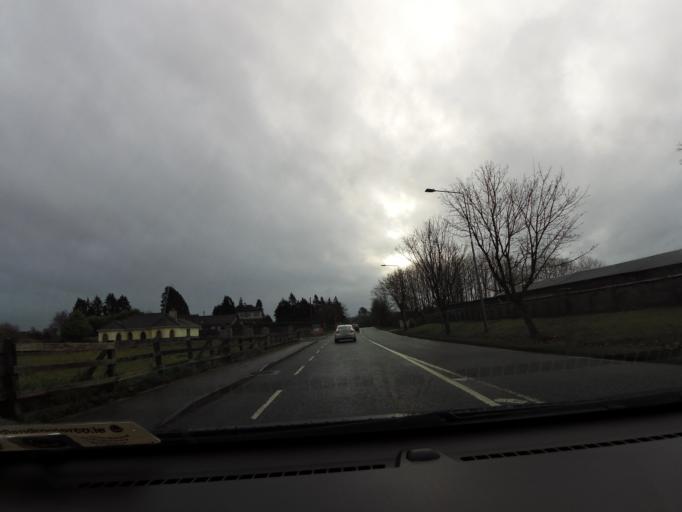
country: IE
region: Munster
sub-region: North Tipperary
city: Roscrea
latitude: 52.9618
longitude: -7.8066
